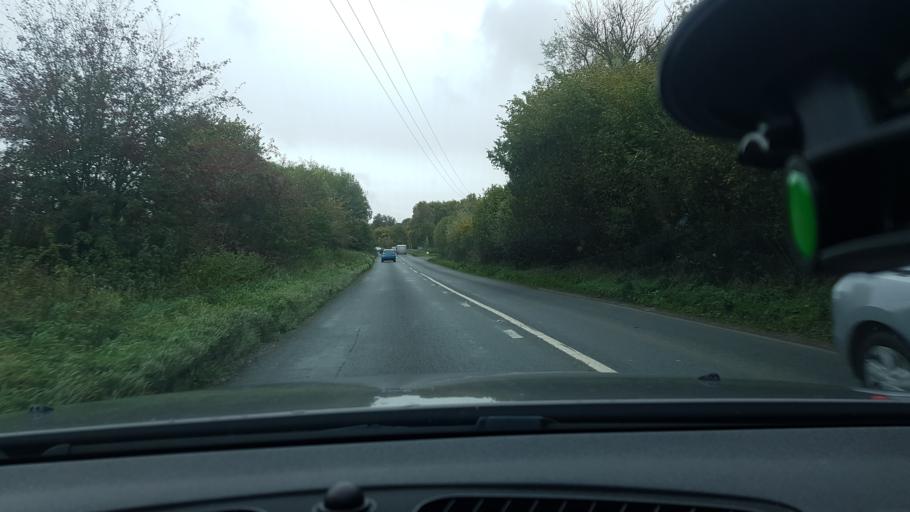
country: GB
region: England
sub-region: Wiltshire
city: Marlborough
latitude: 51.4391
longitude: -1.7322
